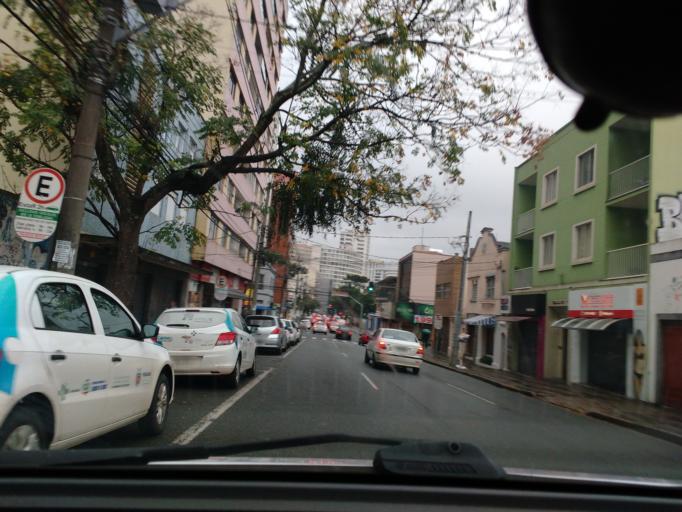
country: BR
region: Parana
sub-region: Curitiba
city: Curitiba
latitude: -25.4258
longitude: -49.2624
